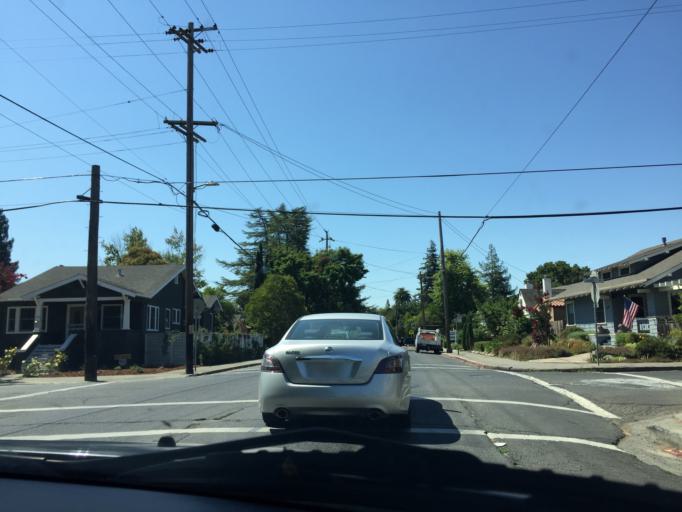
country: US
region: California
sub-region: Napa County
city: Napa
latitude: 38.2929
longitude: -122.2942
